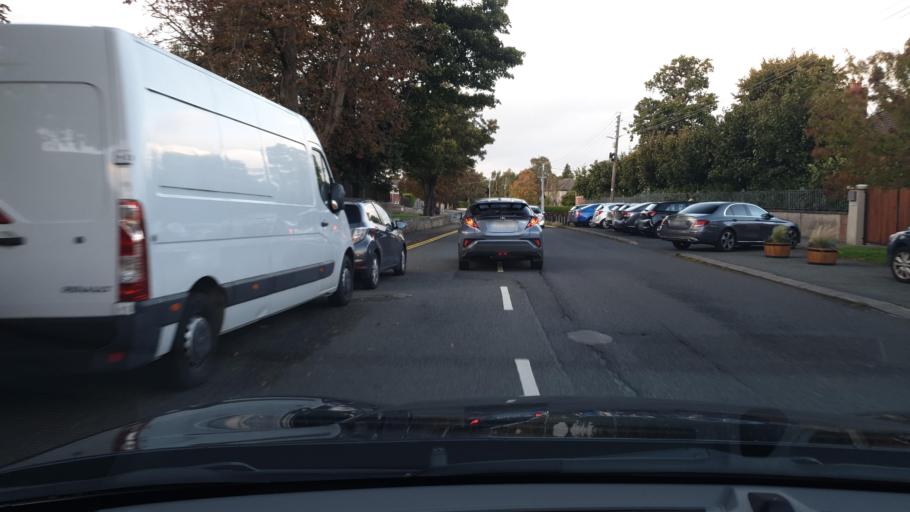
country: IE
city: Booterstown
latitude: 53.2923
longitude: -6.1921
